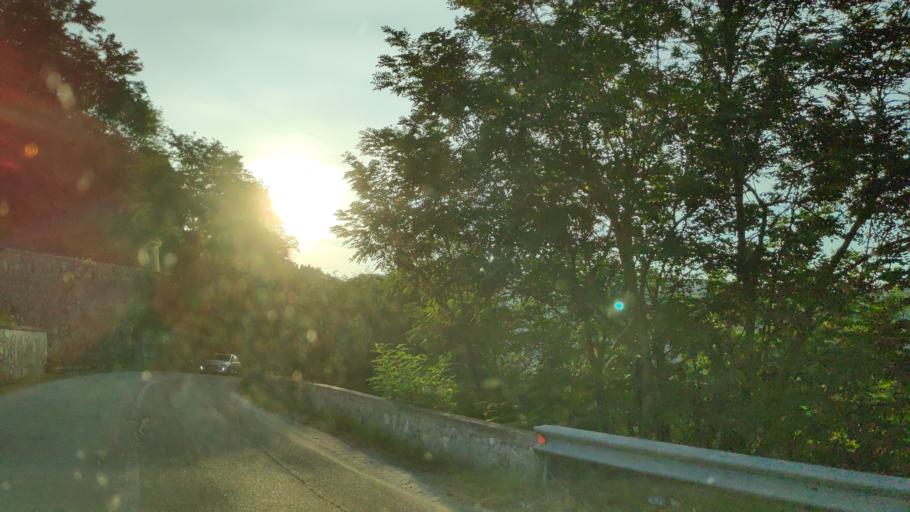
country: IT
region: Calabria
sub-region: Provincia di Catanzaro
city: Satriano
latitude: 38.6704
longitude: 16.4867
